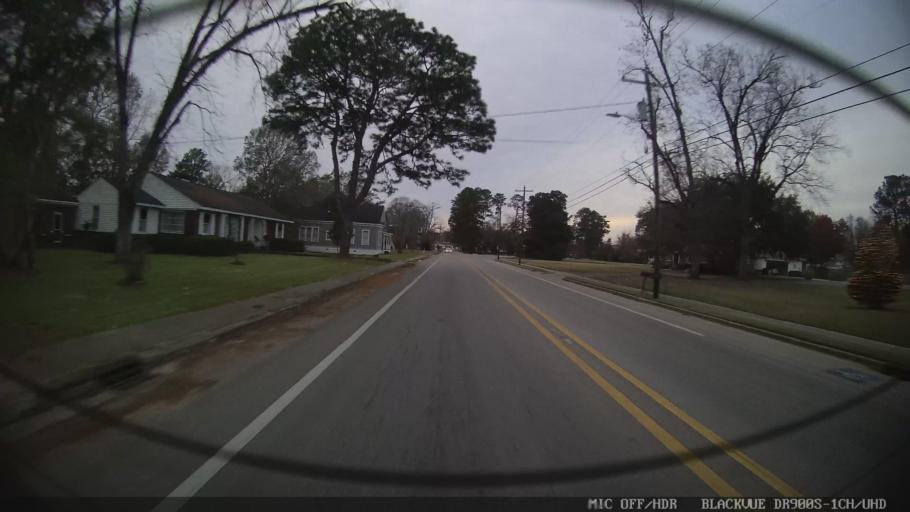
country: US
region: Mississippi
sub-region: Clarke County
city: Quitman
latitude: 32.0365
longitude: -88.7241
